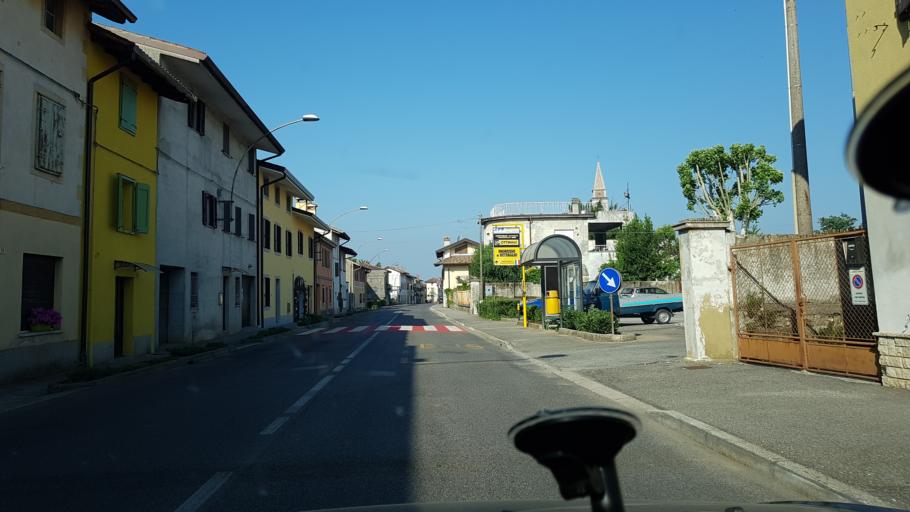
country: IT
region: Friuli Venezia Giulia
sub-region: Provincia di Gorizia
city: San Lorenzo Isontino
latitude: 45.9308
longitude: 13.5297
